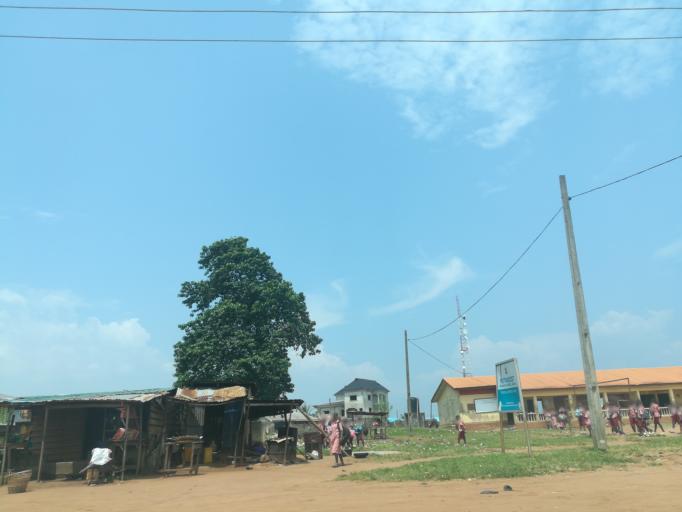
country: NG
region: Lagos
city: Ikorodu
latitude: 6.5771
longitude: 3.6286
